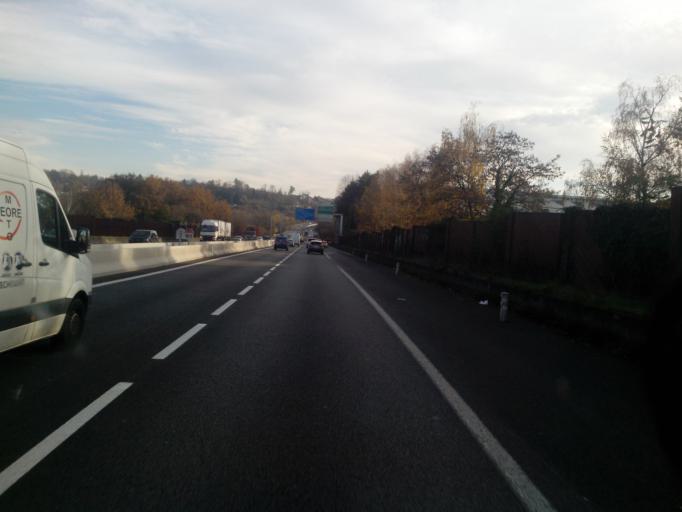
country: FR
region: Limousin
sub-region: Departement de la Haute-Vienne
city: Limoges
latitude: 45.8416
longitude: 1.2796
